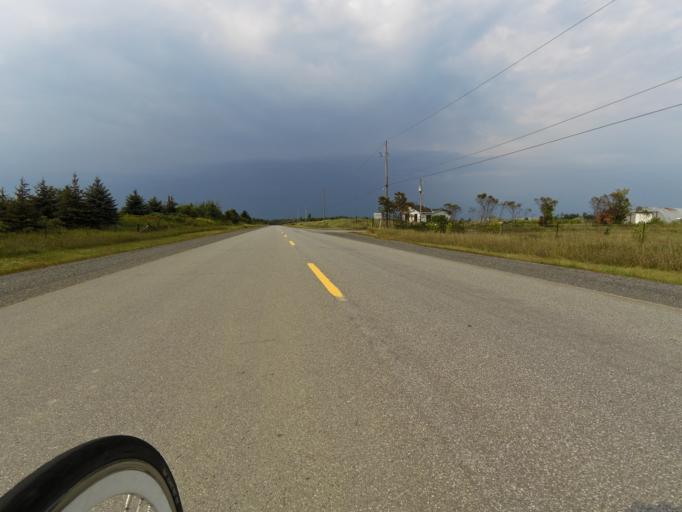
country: CA
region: Ontario
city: Bells Corners
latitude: 45.2334
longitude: -75.7521
